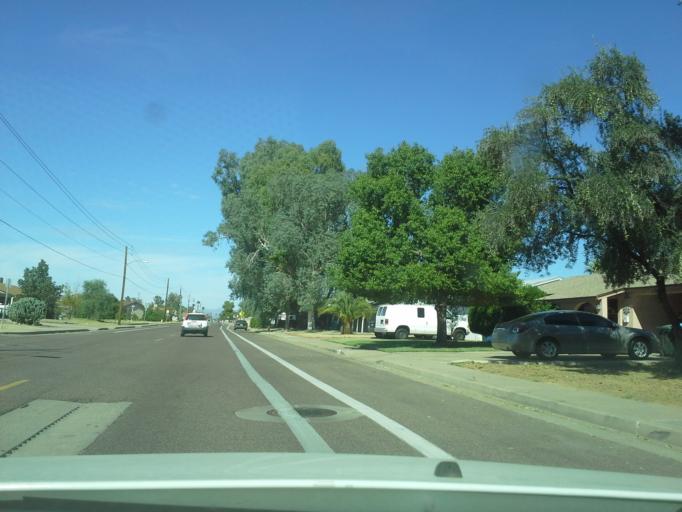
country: US
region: Arizona
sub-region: Maricopa County
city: Paradise Valley
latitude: 33.6089
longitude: -112.0046
